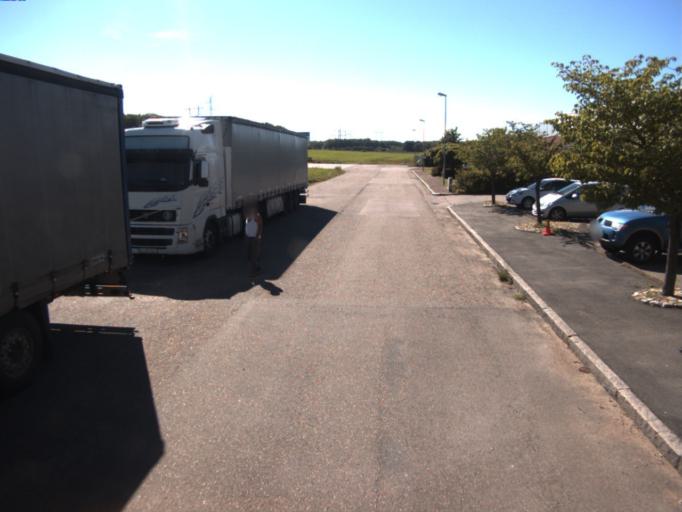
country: SE
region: Skane
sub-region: Helsingborg
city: Odakra
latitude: 56.0924
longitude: 12.7392
